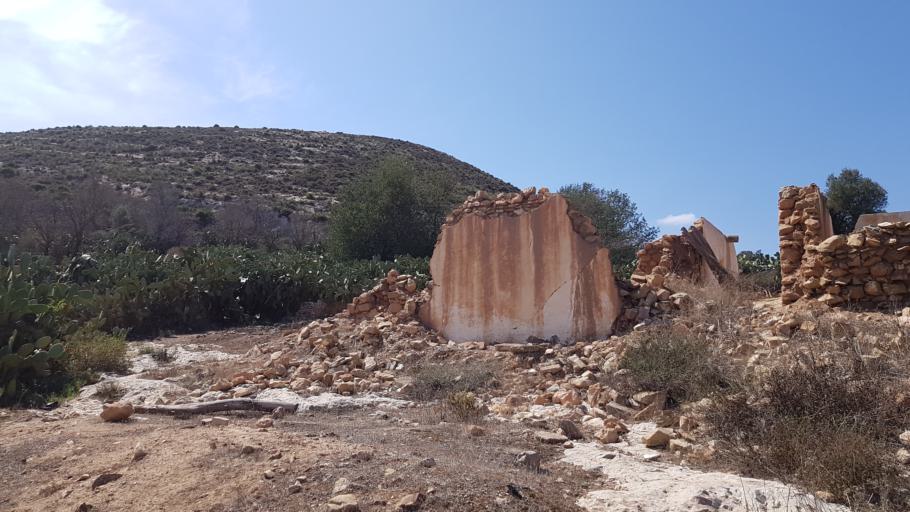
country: MA
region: Taza-Al Hoceima-Taounate
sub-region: Al-Hoceima
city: Rouadi
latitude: 35.1698
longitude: -4.0726
